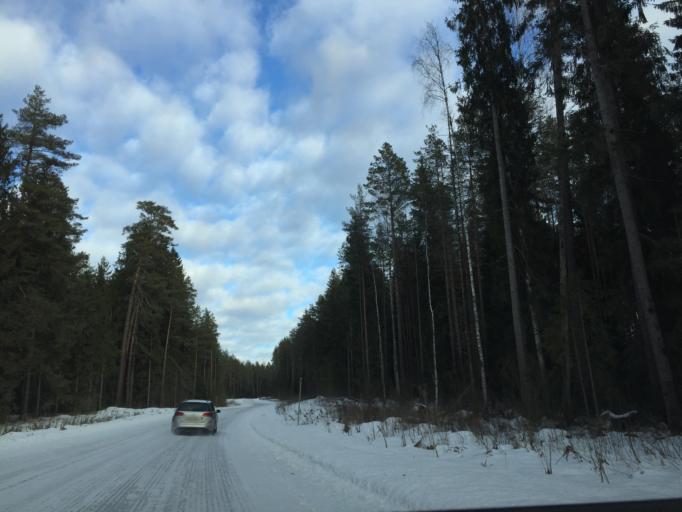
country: LV
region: Ogre
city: Jumprava
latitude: 56.5561
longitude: 24.9008
